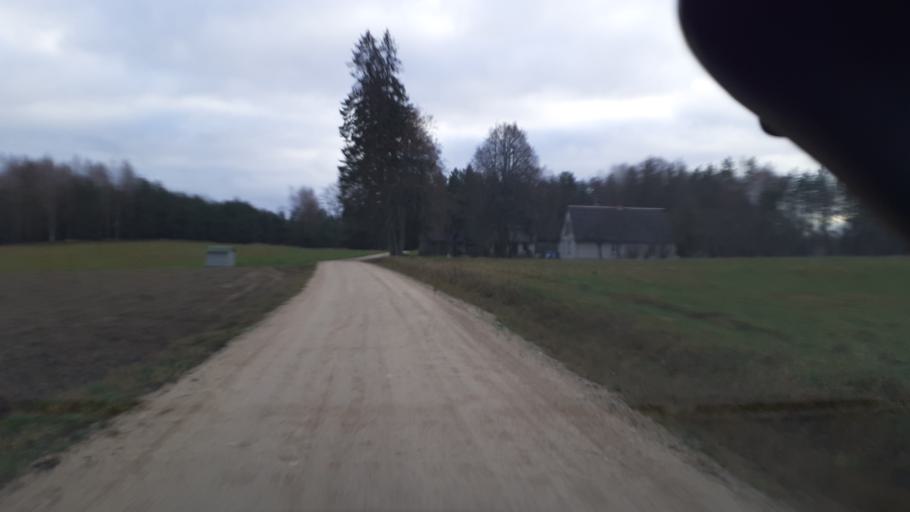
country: LV
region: Kuldigas Rajons
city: Kuldiga
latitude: 56.9054
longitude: 21.9041
